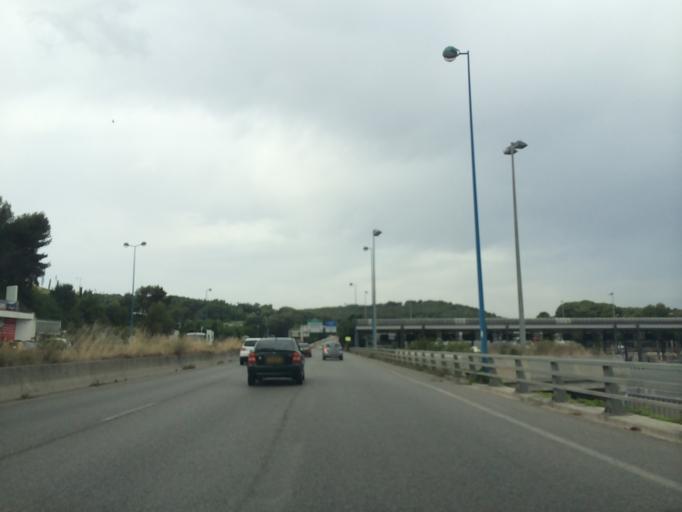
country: FR
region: Provence-Alpes-Cote d'Azur
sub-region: Departement des Alpes-Maritimes
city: Biot
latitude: 43.6023
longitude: 7.0800
